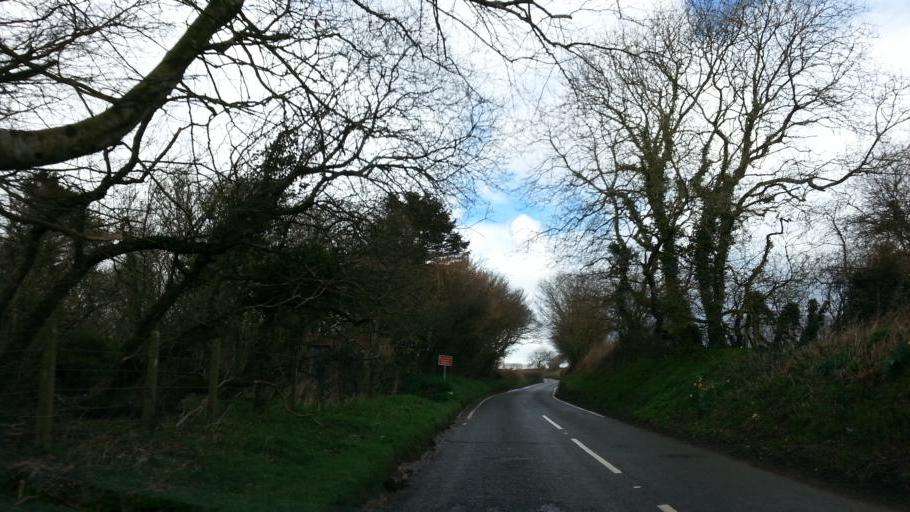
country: GB
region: England
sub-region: Devon
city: Combe Martin
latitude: 51.1310
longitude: -4.0109
